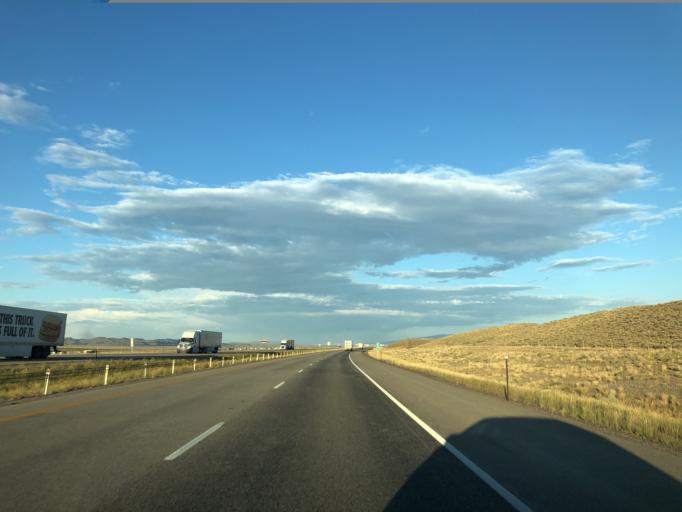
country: US
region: Wyoming
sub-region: Carbon County
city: Rawlins
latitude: 41.7734
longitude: -107.1016
